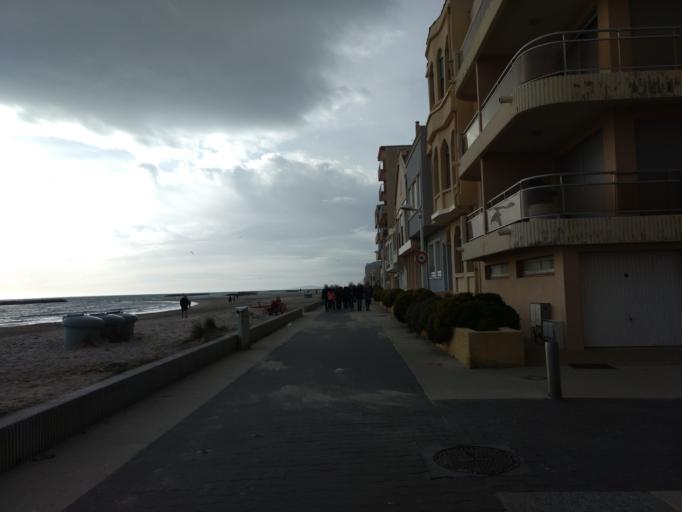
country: FR
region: Languedoc-Roussillon
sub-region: Departement de l'Herault
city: Palavas-les-Flots
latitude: 43.5252
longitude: 3.9271
